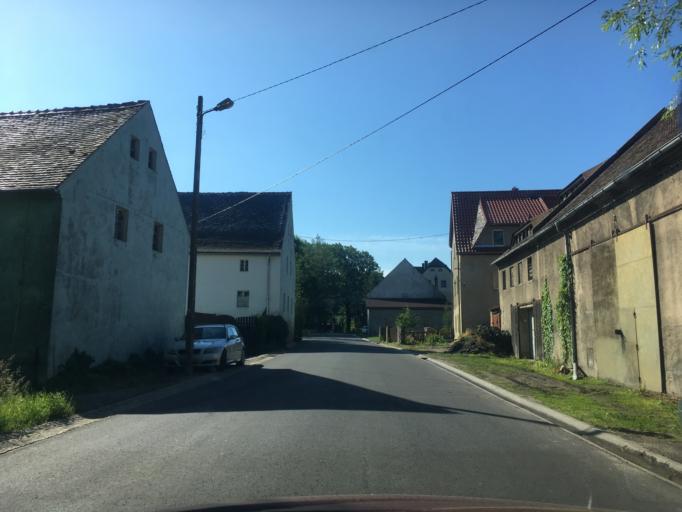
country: PL
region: Lower Silesian Voivodeship
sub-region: Powiat zgorzelecki
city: Sulikow
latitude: 51.0920
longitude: 15.0490
